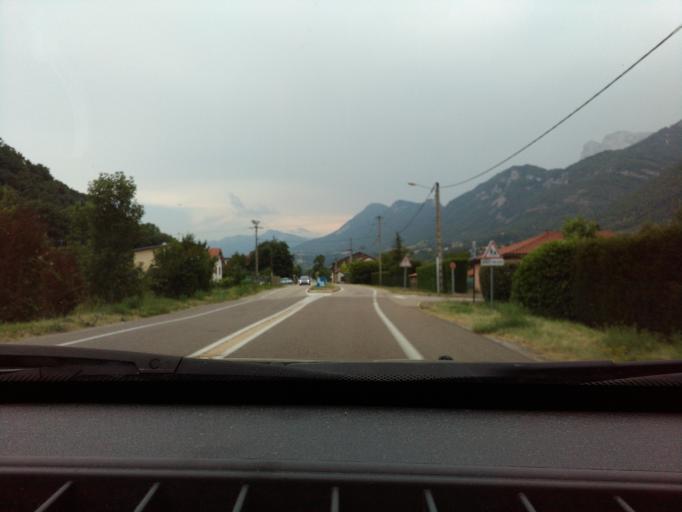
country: FR
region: Rhone-Alpes
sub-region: Departement de l'Isere
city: Vif
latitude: 45.0403
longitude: 5.6621
